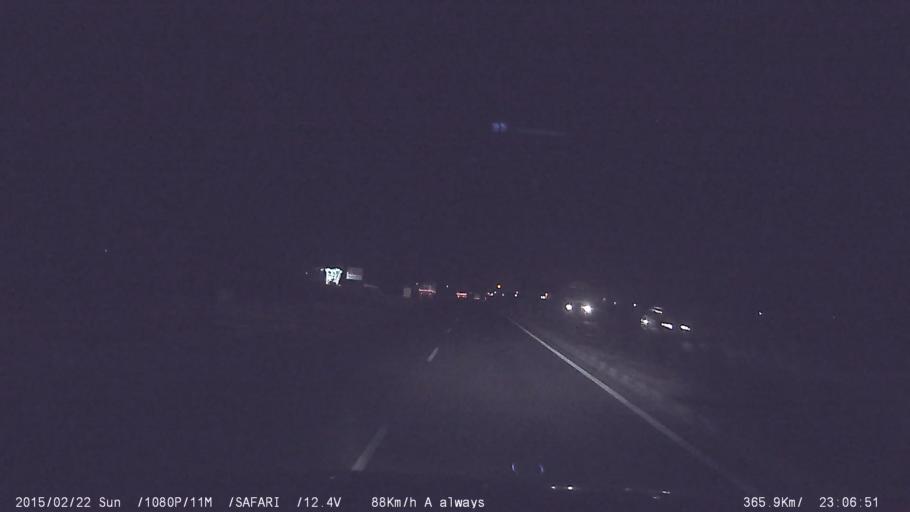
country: IN
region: Tamil Nadu
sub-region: Namakkal
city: Rasipuram
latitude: 11.4331
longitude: 78.1565
